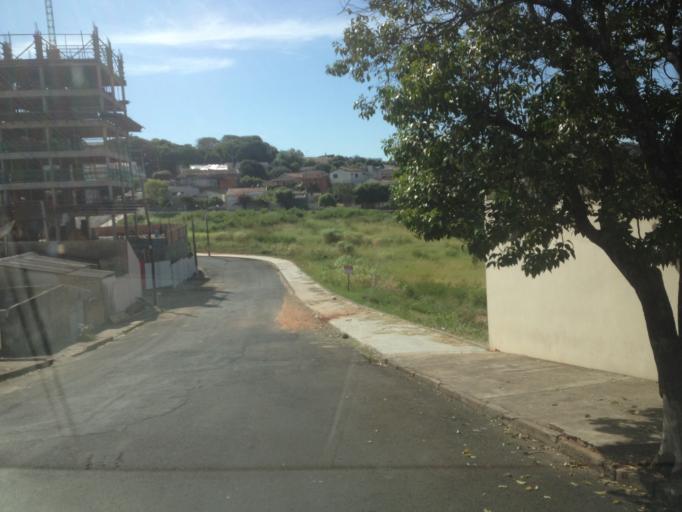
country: BR
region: Sao Paulo
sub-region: Marilia
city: Marilia
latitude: -22.2258
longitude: -49.9445
